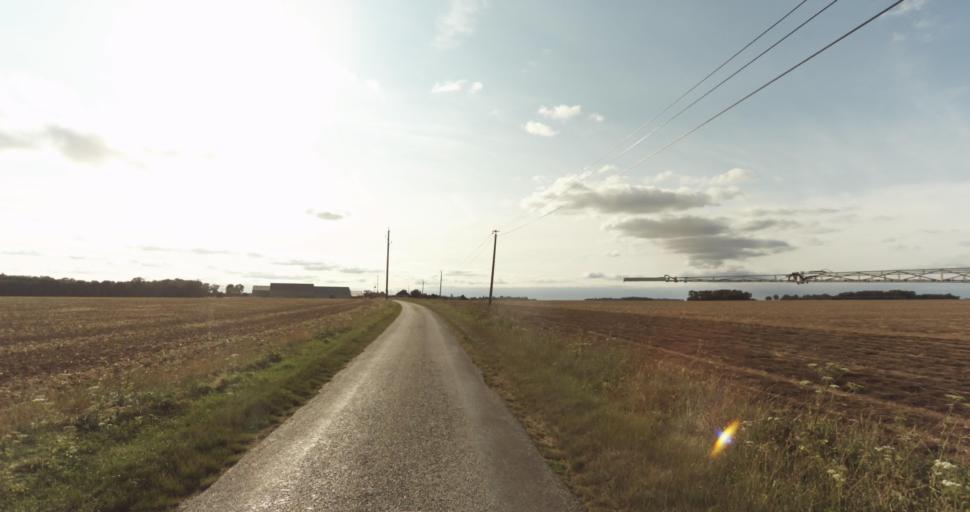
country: FR
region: Haute-Normandie
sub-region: Departement de l'Eure
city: La Couture-Boussey
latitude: 48.9030
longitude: 1.3409
